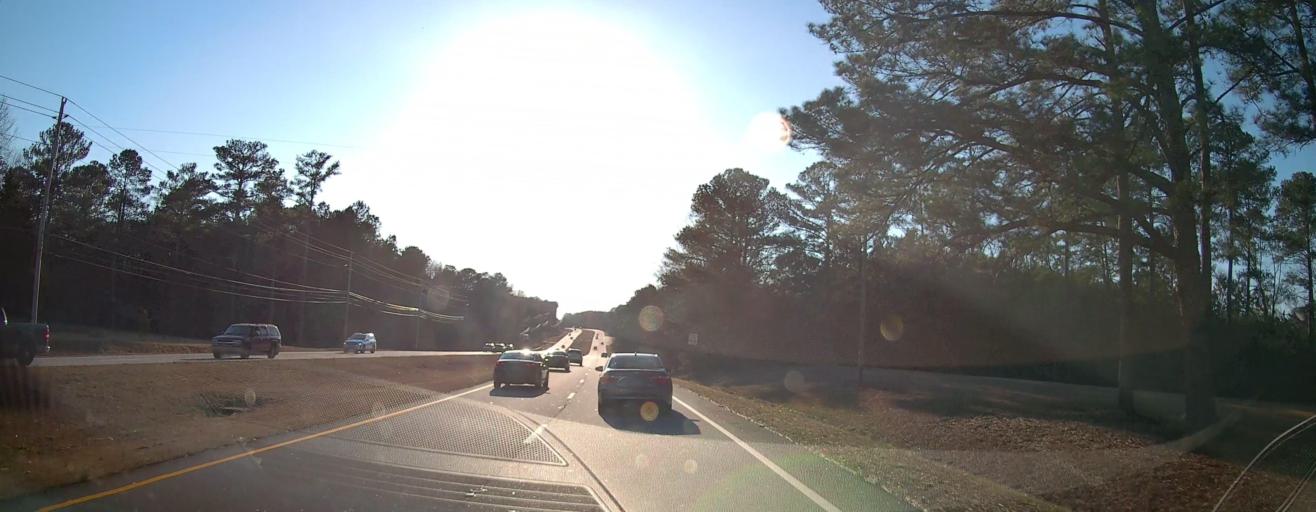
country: US
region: Georgia
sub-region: Fayette County
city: Tyrone
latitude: 33.4421
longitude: -84.5379
